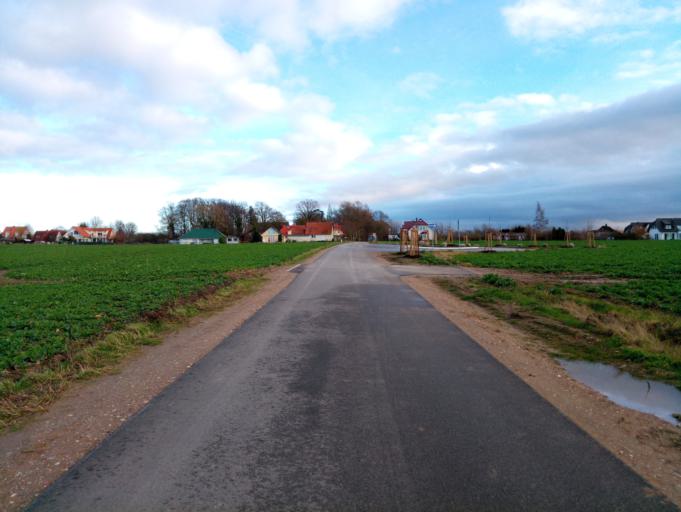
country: DE
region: Mecklenburg-Vorpommern
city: Dassow
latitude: 53.9702
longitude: 10.9613
